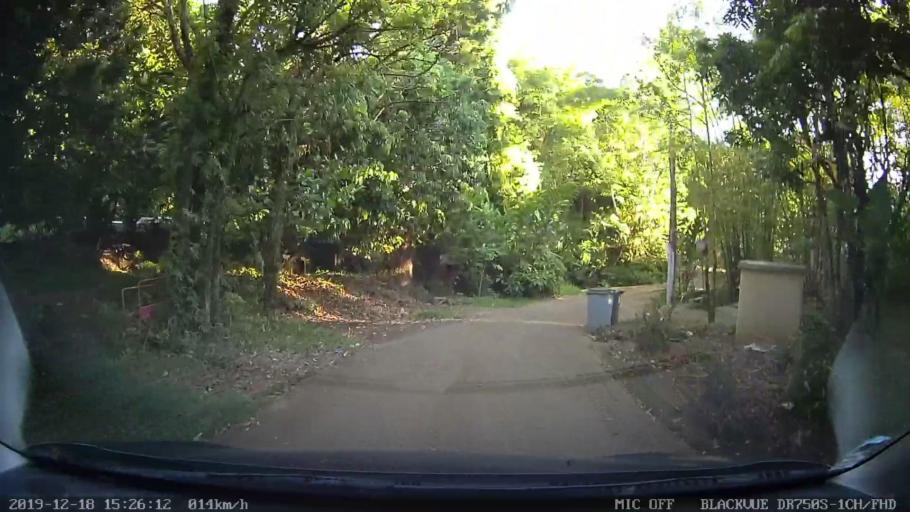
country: RE
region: Reunion
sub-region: Reunion
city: Bras-Panon
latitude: -21.0024
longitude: 55.6521
